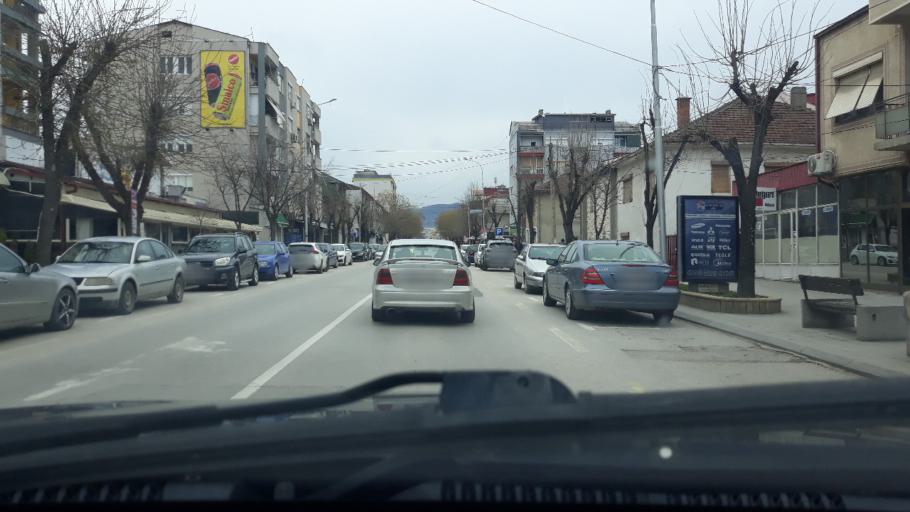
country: MK
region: Kavadarci
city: Kavadarci
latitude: 41.4372
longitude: 22.0107
